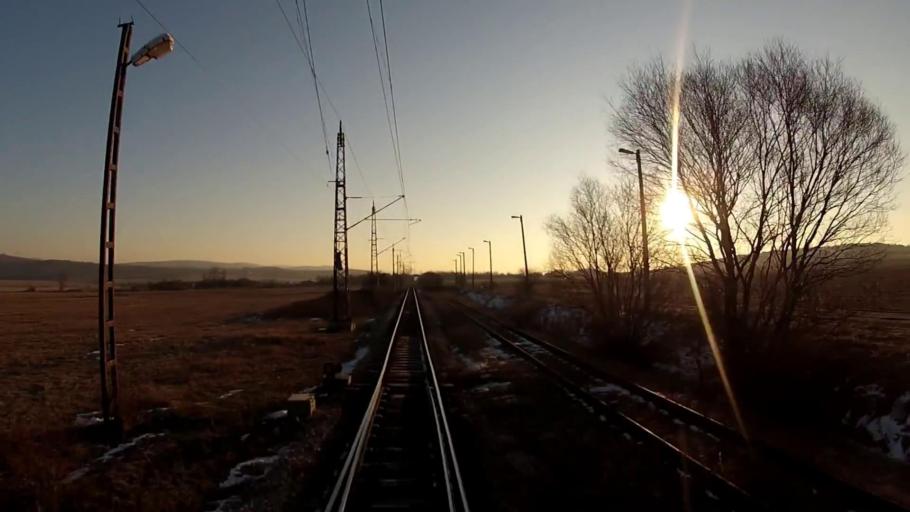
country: BG
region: Sofiya
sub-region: Obshtina Slivnitsa
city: Slivnitsa
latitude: 42.8802
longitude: 23.0150
